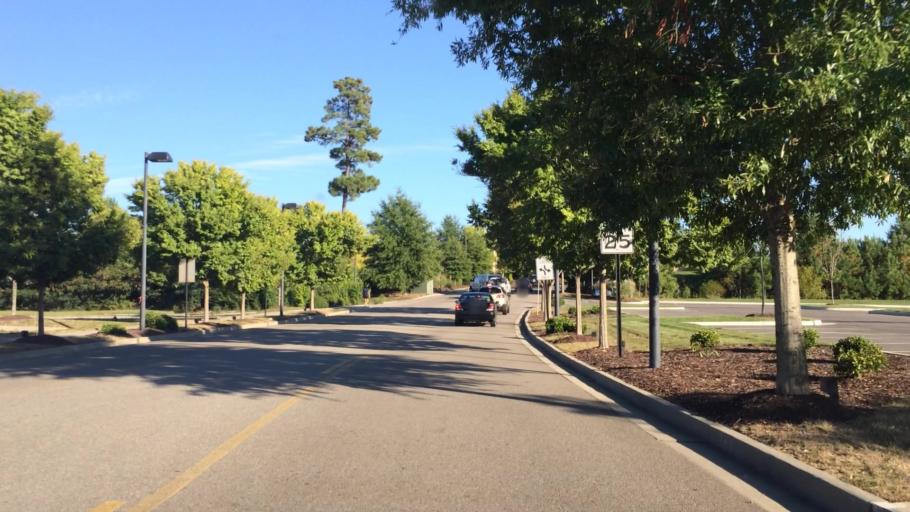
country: US
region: Virginia
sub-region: Henrico County
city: Short Pump
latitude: 37.6585
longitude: -77.6250
